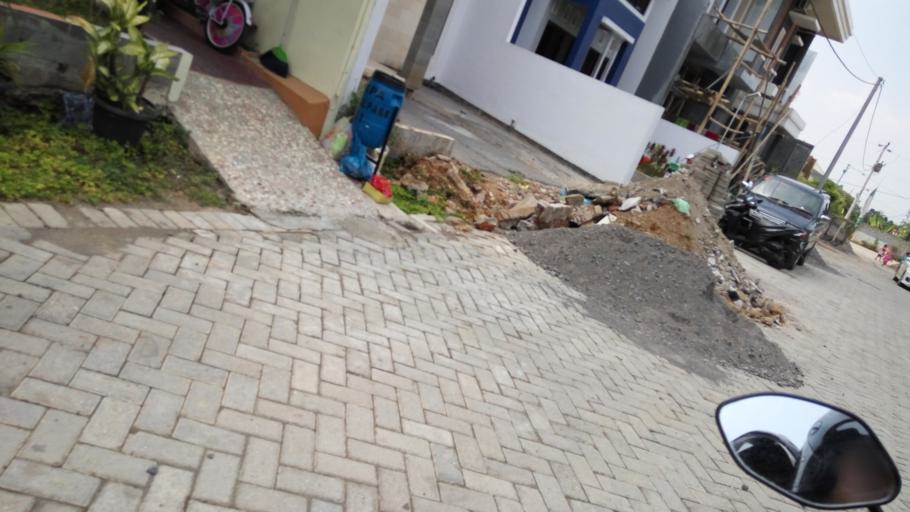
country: ID
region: Central Java
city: Mranggen
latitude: -7.0415
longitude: 110.4798
